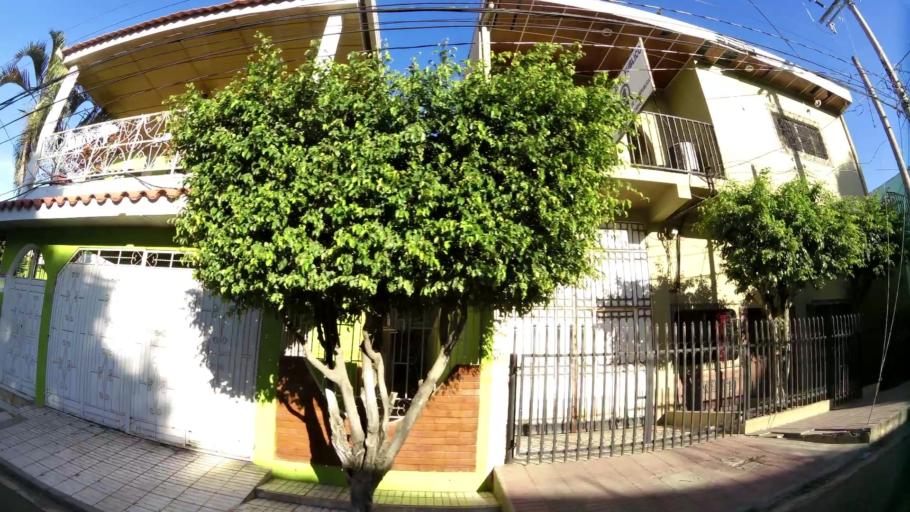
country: SV
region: Santa Ana
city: Metapan
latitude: 14.3342
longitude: -89.4480
